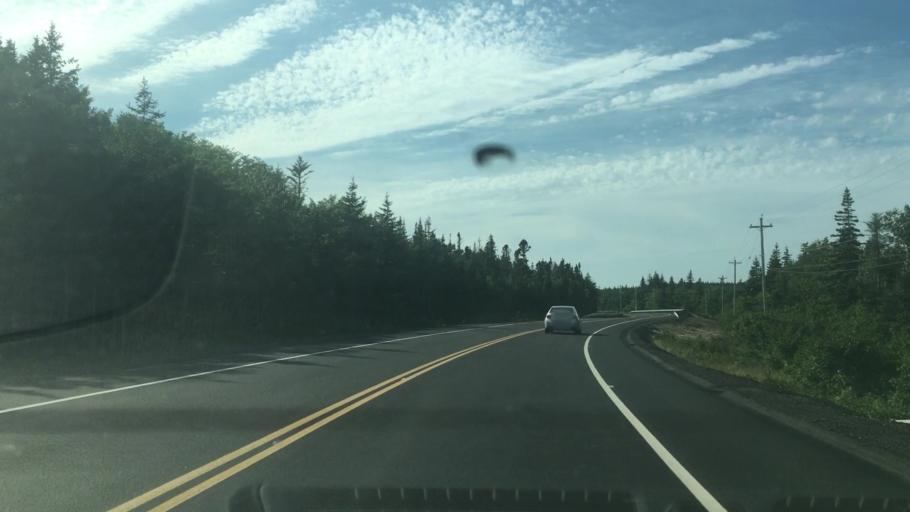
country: CA
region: Nova Scotia
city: Sydney Mines
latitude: 46.8406
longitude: -60.3909
